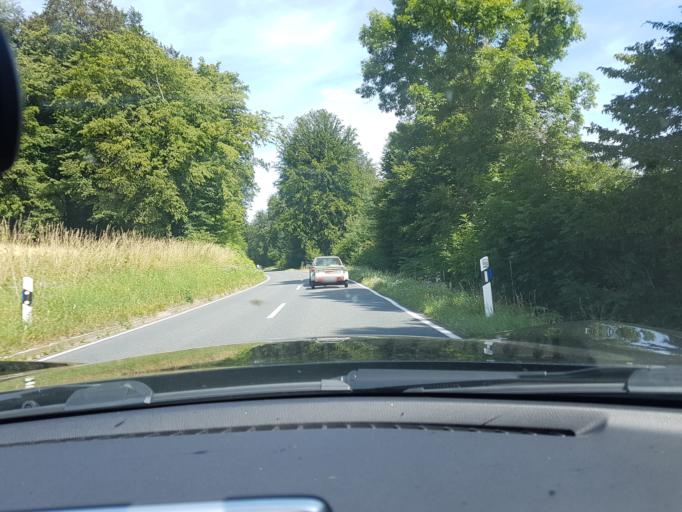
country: DE
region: Baden-Wuerttemberg
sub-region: Karlsruhe Region
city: Fahrenbach
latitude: 49.4600
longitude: 9.1659
